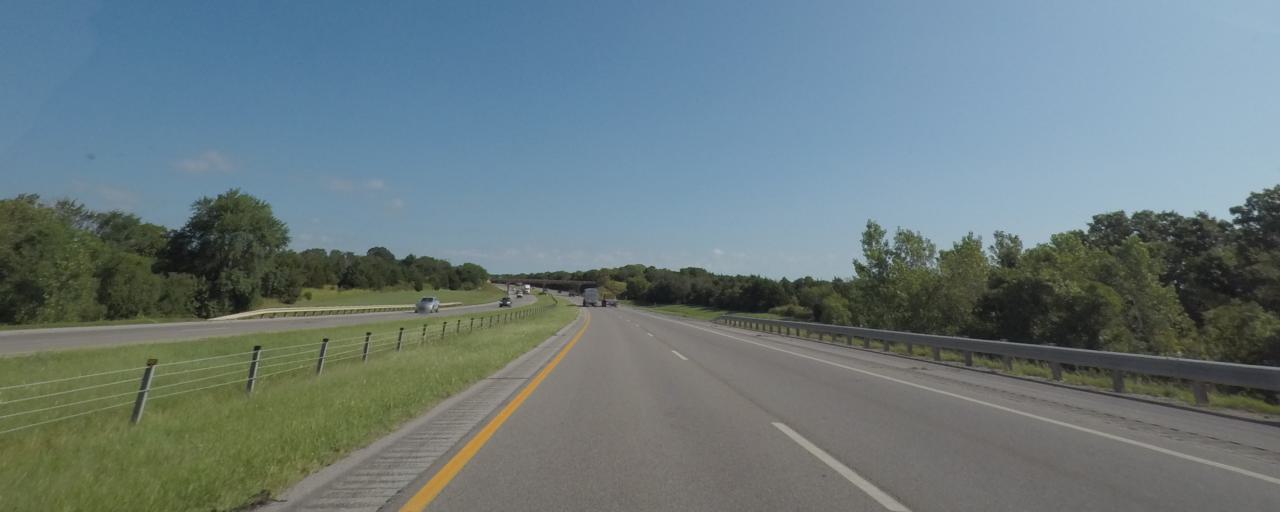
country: US
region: Oklahoma
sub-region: Logan County
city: Guthrie
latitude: 35.8389
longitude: -97.3959
